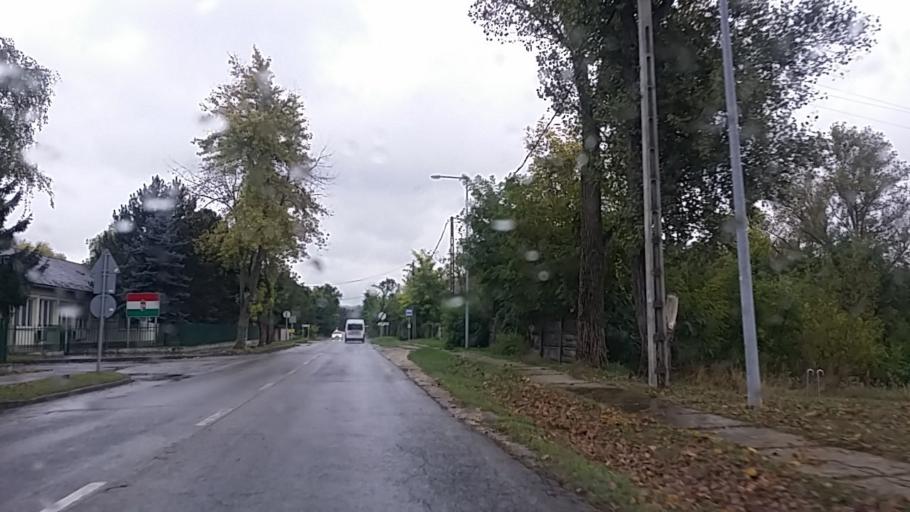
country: HU
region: Komarom-Esztergom
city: Esztergom
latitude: 47.7739
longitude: 18.7551
